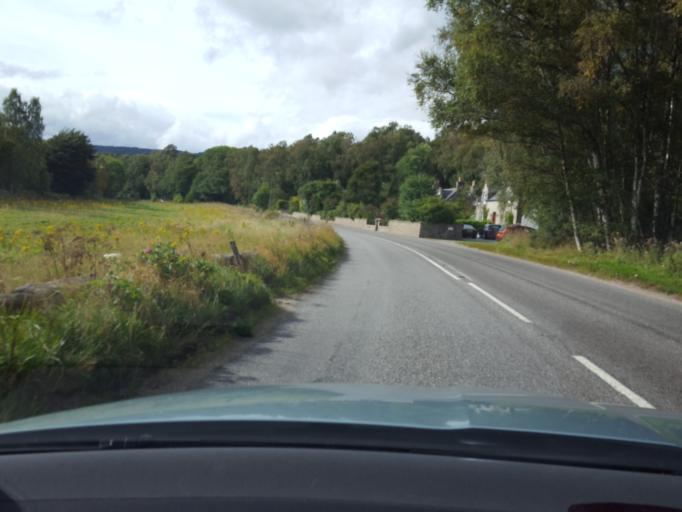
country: GB
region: Scotland
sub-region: Aberdeenshire
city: Ballater
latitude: 57.0712
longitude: -2.9683
